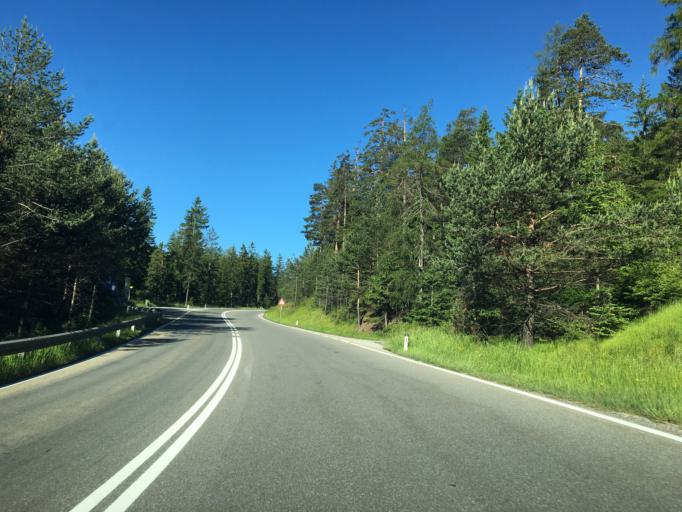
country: AT
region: Tyrol
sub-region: Politischer Bezirk Reutte
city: Biberwier
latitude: 47.3628
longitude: 10.8664
